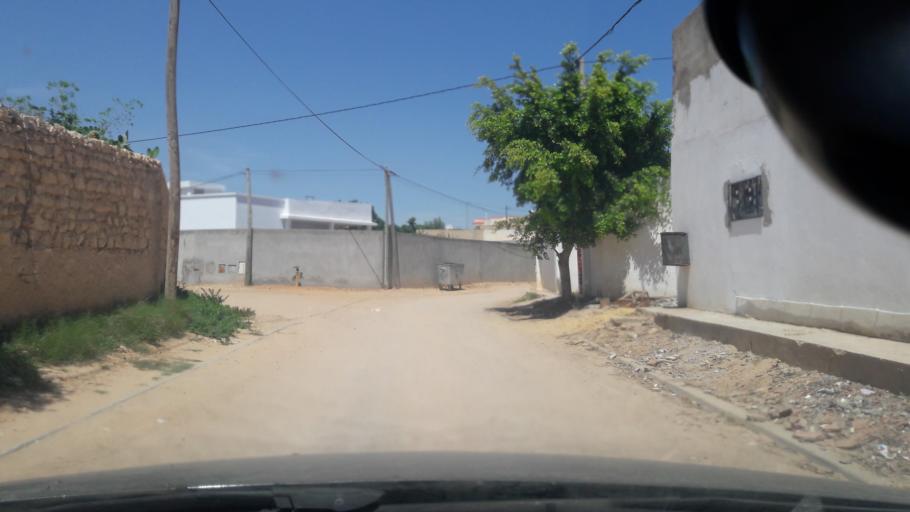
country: TN
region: Safaqis
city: Al Qarmadah
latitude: 34.8115
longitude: 10.7530
